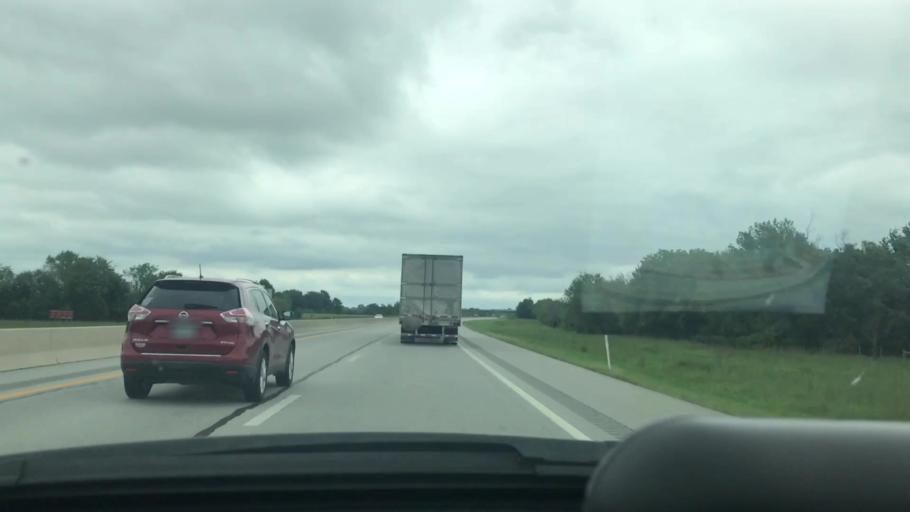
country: US
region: Oklahoma
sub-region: Ottawa County
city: Miami
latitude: 36.8926
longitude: -94.8296
